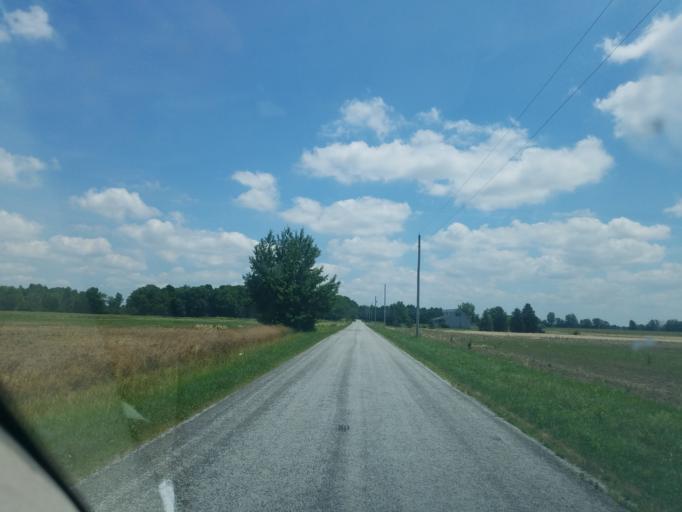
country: US
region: Ohio
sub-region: Hardin County
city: Forest
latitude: 40.7752
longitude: -83.6197
